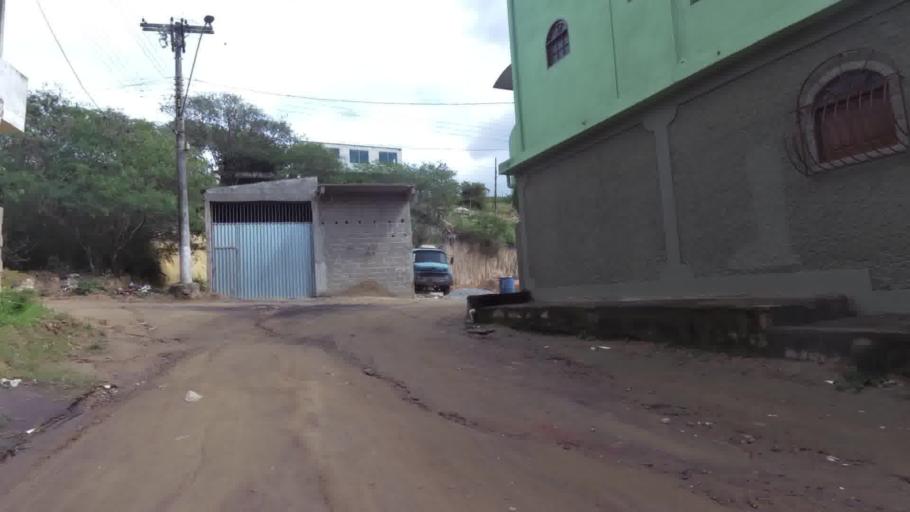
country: BR
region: Espirito Santo
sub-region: Marataizes
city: Marataizes
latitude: -21.0285
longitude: -40.8188
